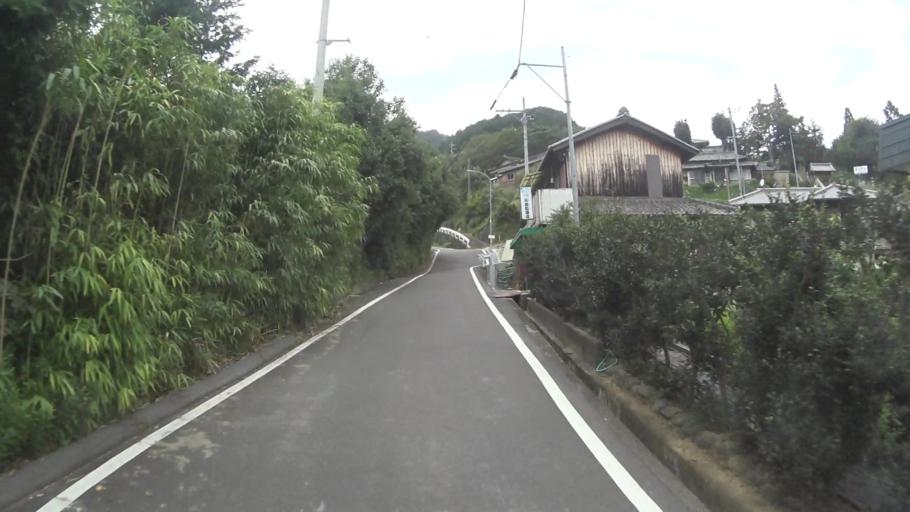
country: JP
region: Kyoto
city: Tanabe
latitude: 34.7968
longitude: 135.8850
